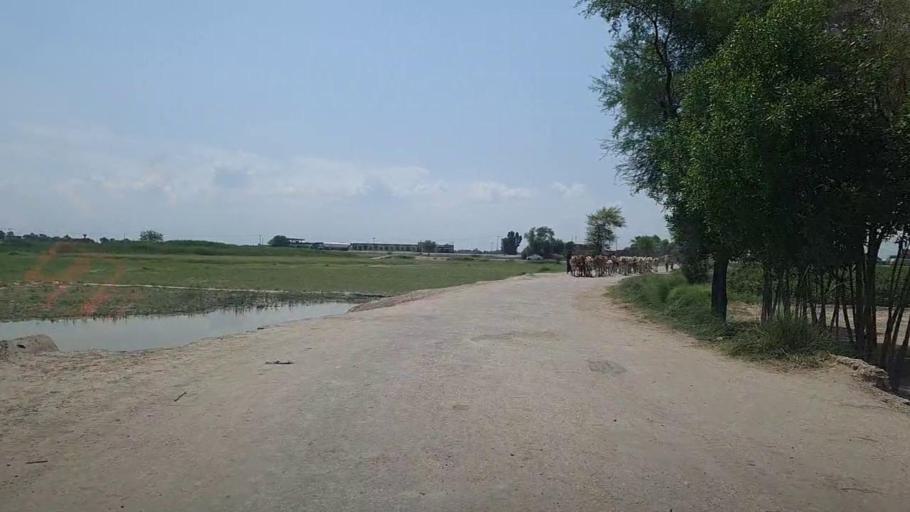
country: PK
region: Sindh
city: Ubauro
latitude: 28.1863
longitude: 69.7998
